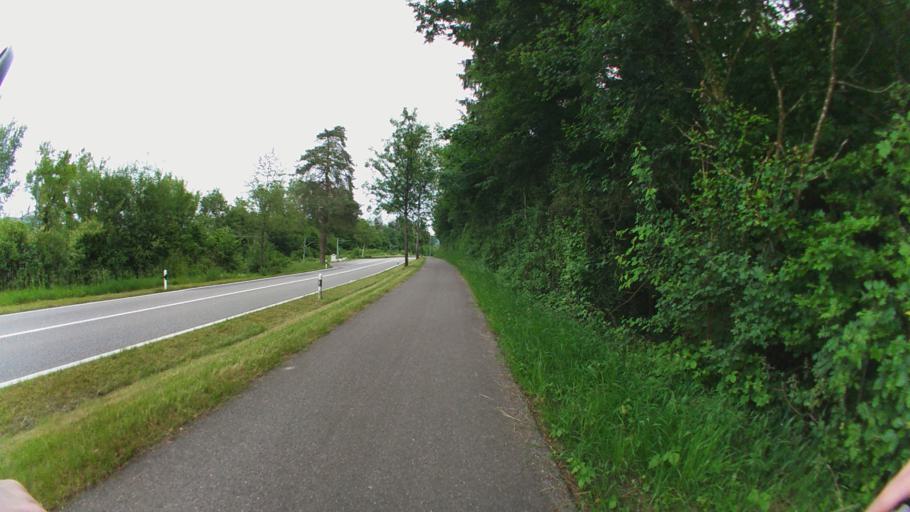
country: CH
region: Aargau
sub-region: Bezirk Zurzach
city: Koblenz
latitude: 47.6079
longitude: 8.2653
